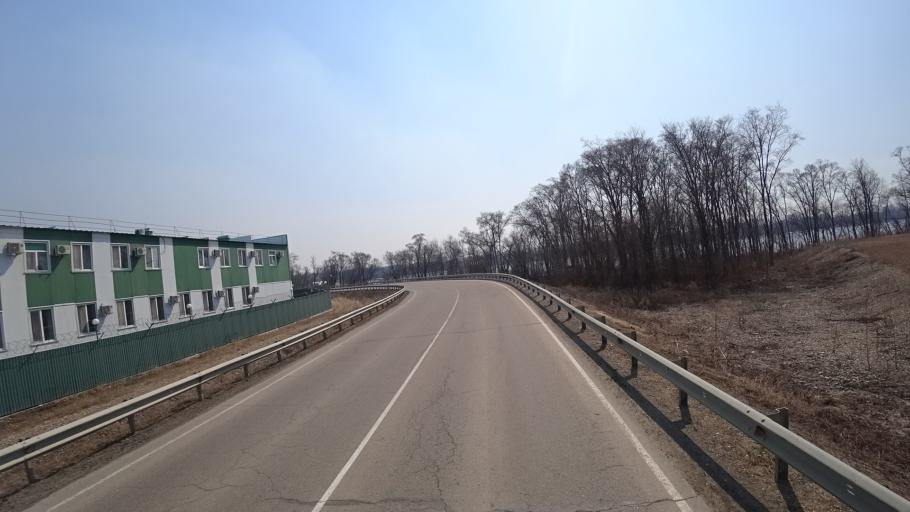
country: RU
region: Amur
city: Novobureyskiy
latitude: 49.7838
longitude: 129.9223
